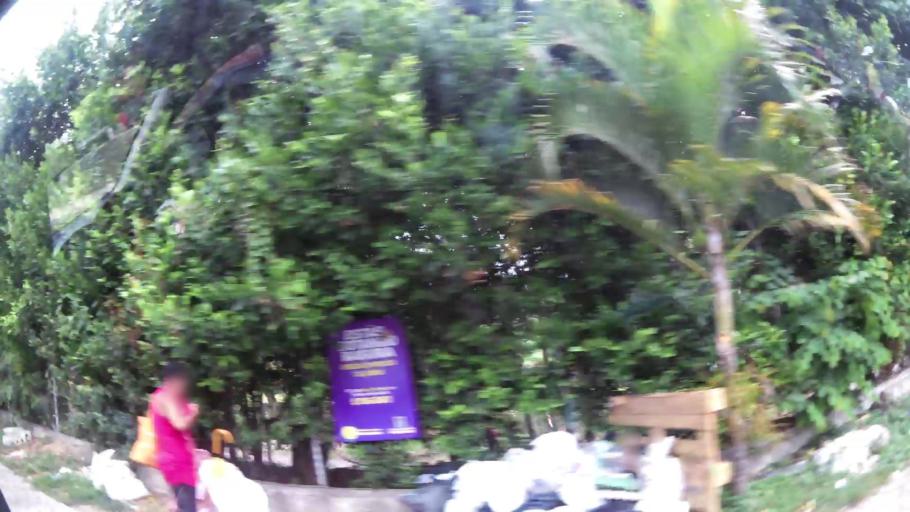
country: CO
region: Antioquia
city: Itagui
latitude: 6.2019
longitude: -75.5912
